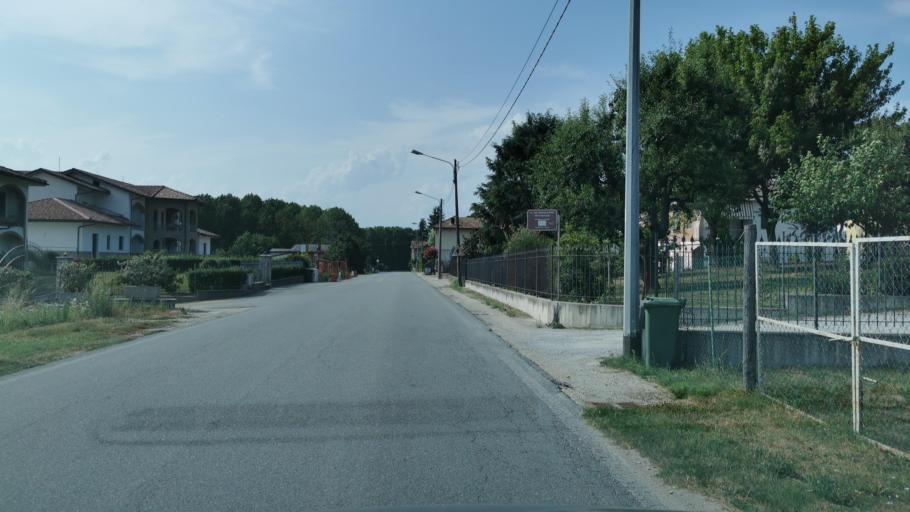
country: IT
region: Piedmont
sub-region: Provincia di Cuneo
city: Grinzane Cavour
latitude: 44.6457
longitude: 7.9977
